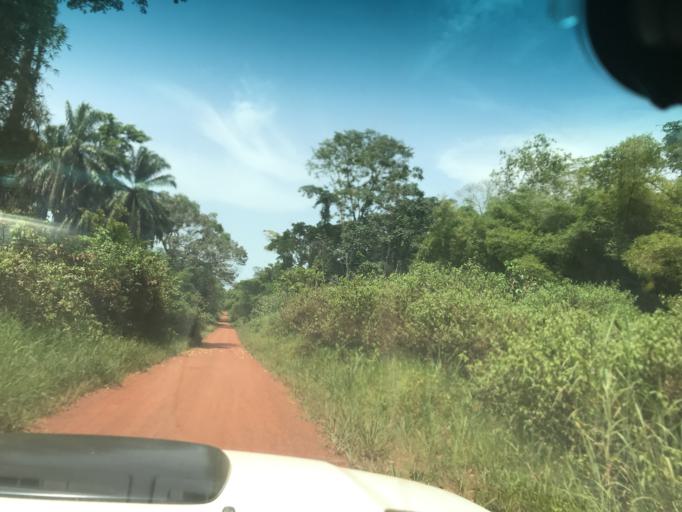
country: CD
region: Eastern Province
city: Aketi
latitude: 2.8737
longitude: 23.9530
